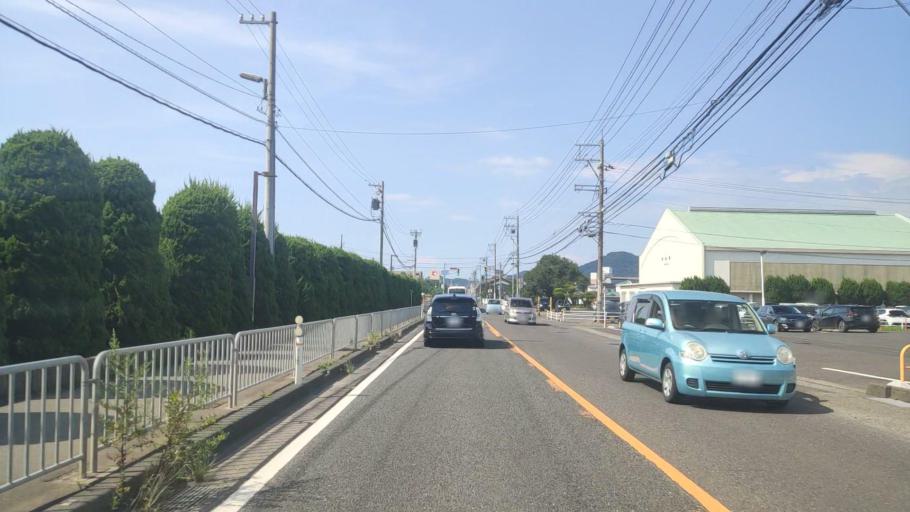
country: JP
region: Fukui
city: Tsuruga
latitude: 35.6387
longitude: 136.0707
